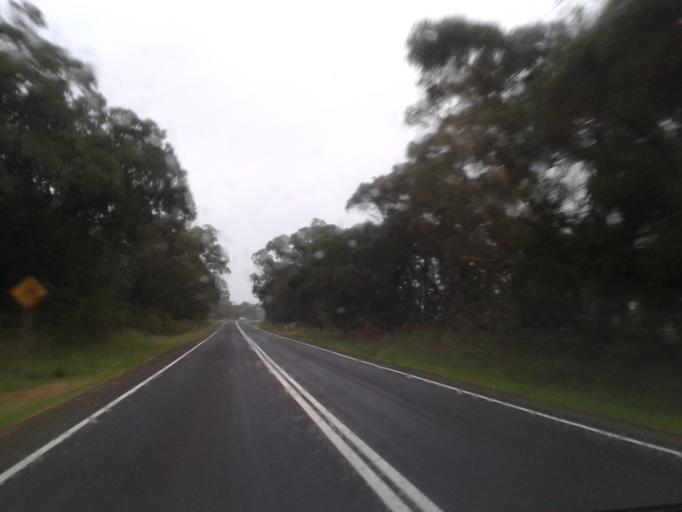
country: AU
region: Victoria
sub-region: Glenelg
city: Portland
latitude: -38.2361
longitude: 141.4572
